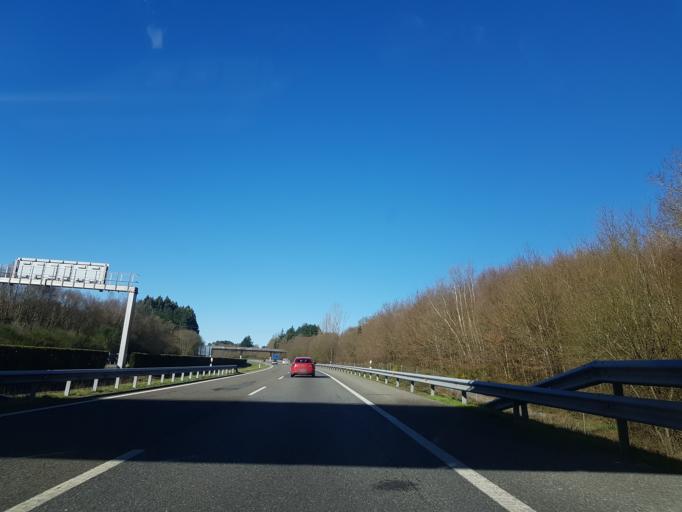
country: ES
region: Galicia
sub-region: Provincia de Lugo
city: Rabade
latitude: 43.1353
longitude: -7.6367
